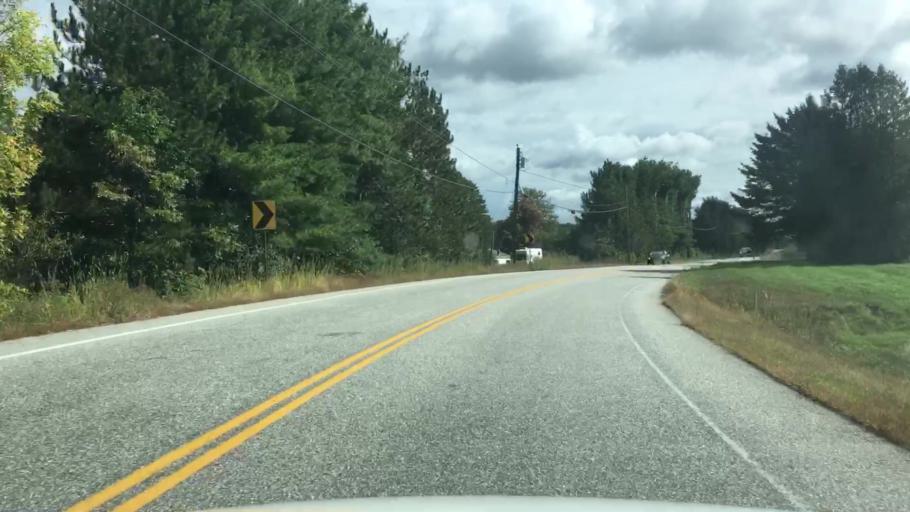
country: US
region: Maine
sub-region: Androscoggin County
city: Lisbon
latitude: 44.0208
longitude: -70.1758
